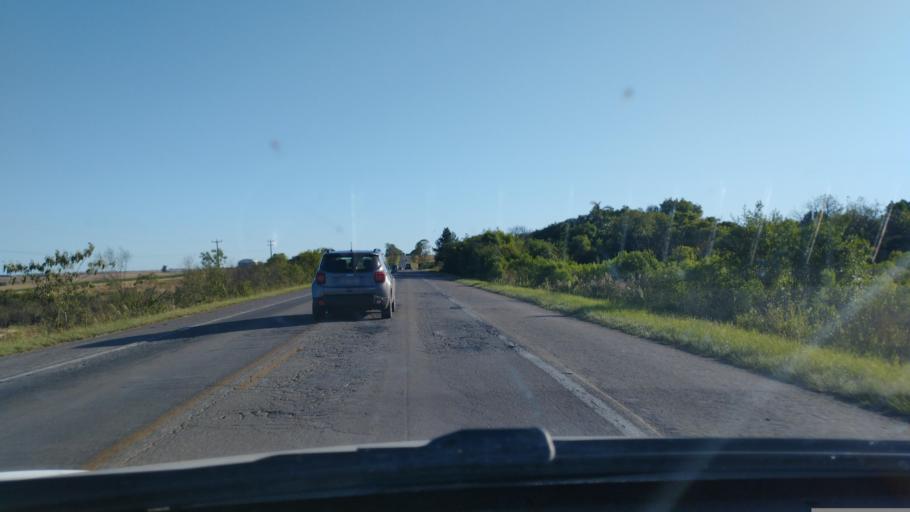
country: BR
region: Rio Grande do Sul
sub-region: Julio De Castilhos
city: Julio de Castilhos
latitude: -29.4176
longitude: -53.6715
